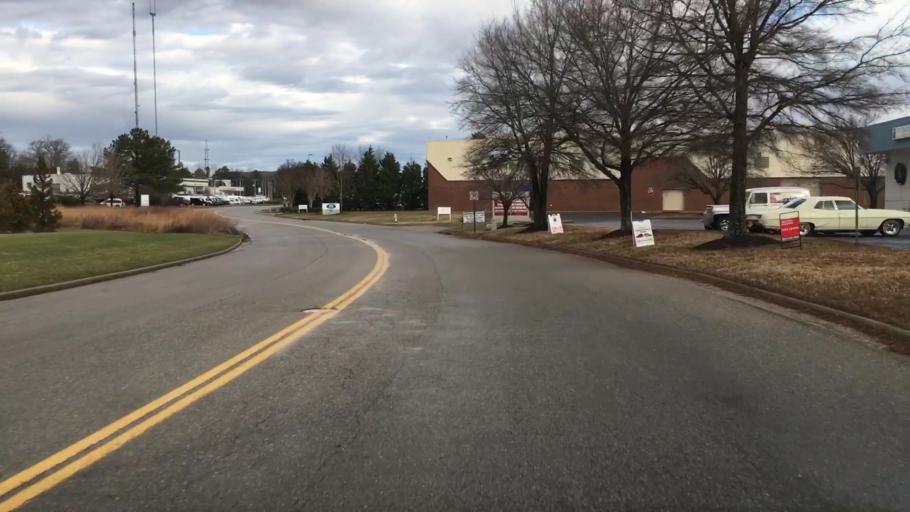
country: US
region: Virginia
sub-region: Chesterfield County
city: Bon Air
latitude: 37.5027
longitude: -77.5917
